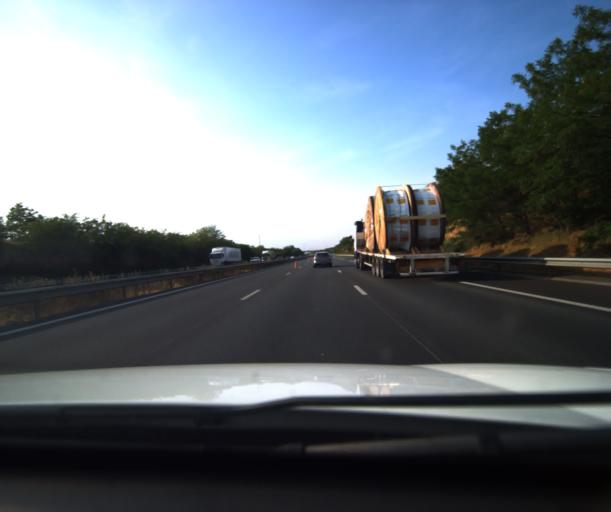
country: FR
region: Midi-Pyrenees
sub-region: Departement de la Haute-Garonne
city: Saint-Alban
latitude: 43.6840
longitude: 1.4132
